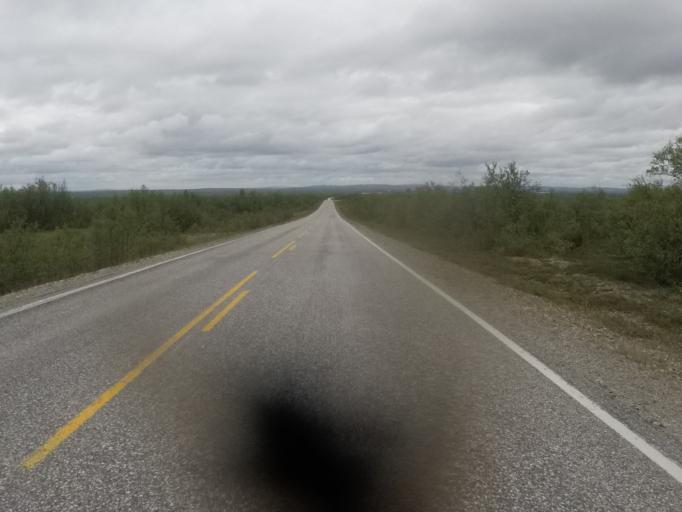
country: NO
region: Finnmark Fylke
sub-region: Kautokeino
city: Kautokeino
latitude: 68.7280
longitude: 23.3082
